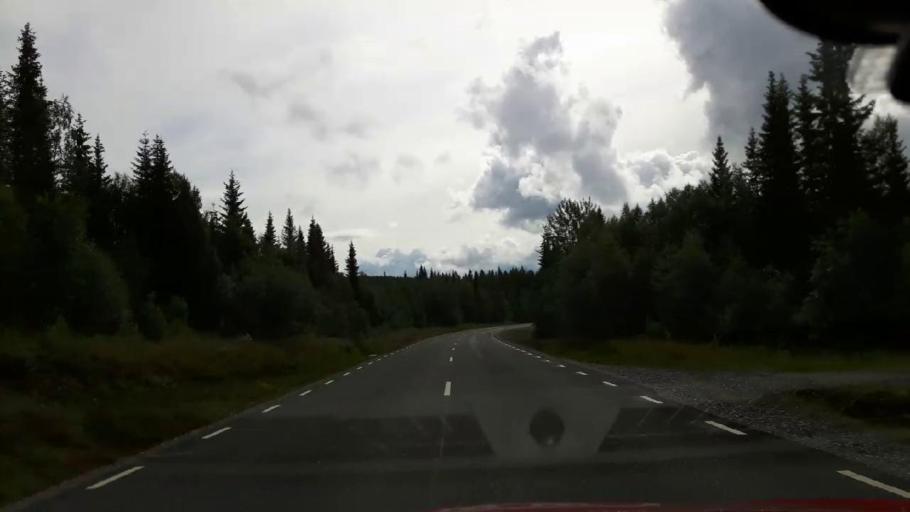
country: NO
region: Nord-Trondelag
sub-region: Lierne
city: Sandvika
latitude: 64.6183
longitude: 14.1228
